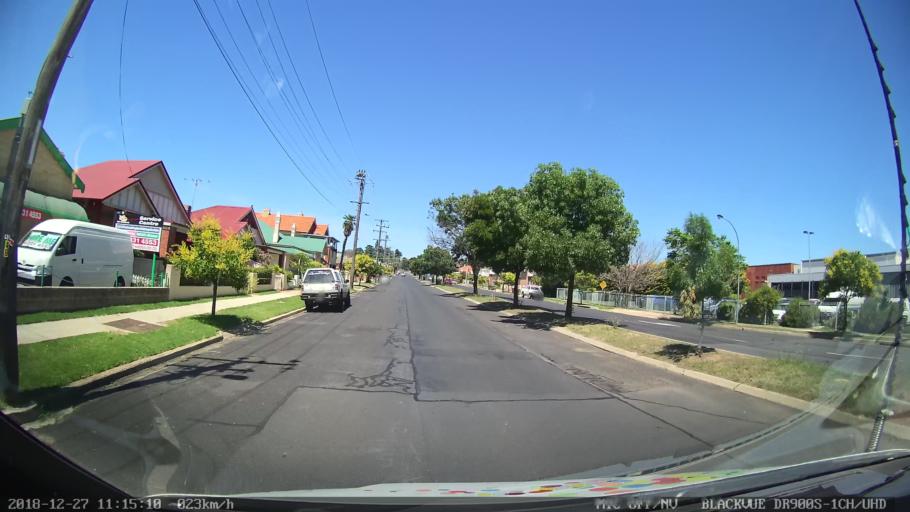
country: AU
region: New South Wales
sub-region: Bathurst Regional
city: Bathurst
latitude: -33.4217
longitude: 149.5752
